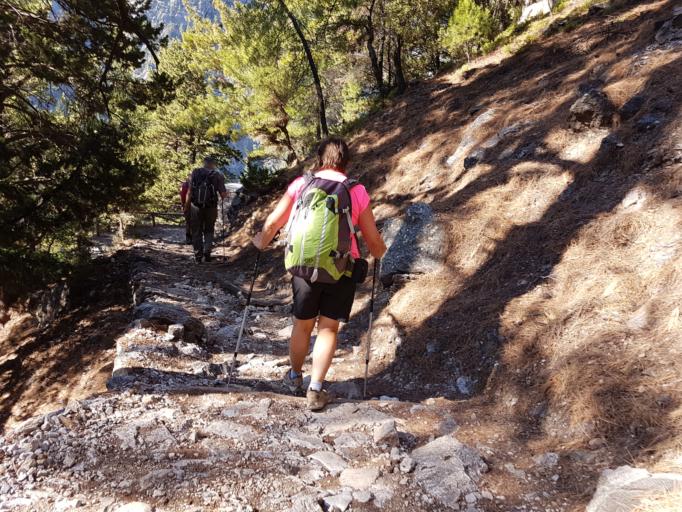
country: GR
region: Crete
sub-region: Nomos Chanias
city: Perivolia
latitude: 35.3093
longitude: 23.9244
